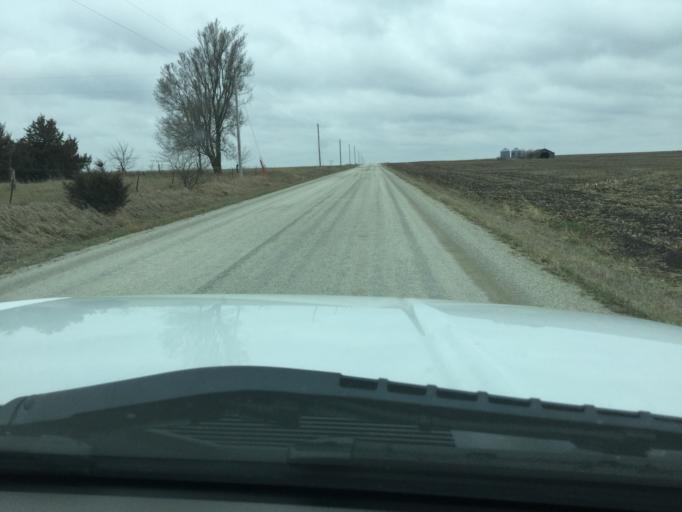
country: US
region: Kansas
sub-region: Nemaha County
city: Sabetha
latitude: 39.7981
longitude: -95.7713
